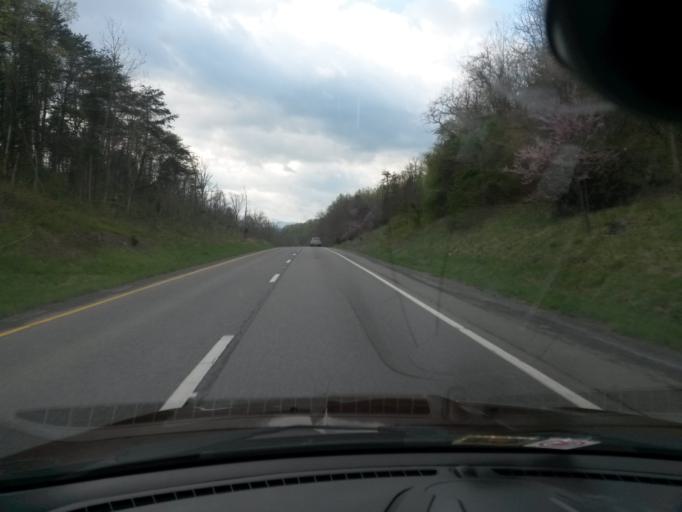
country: US
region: Virginia
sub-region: Botetourt County
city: Fincastle
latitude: 37.5962
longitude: -79.8368
